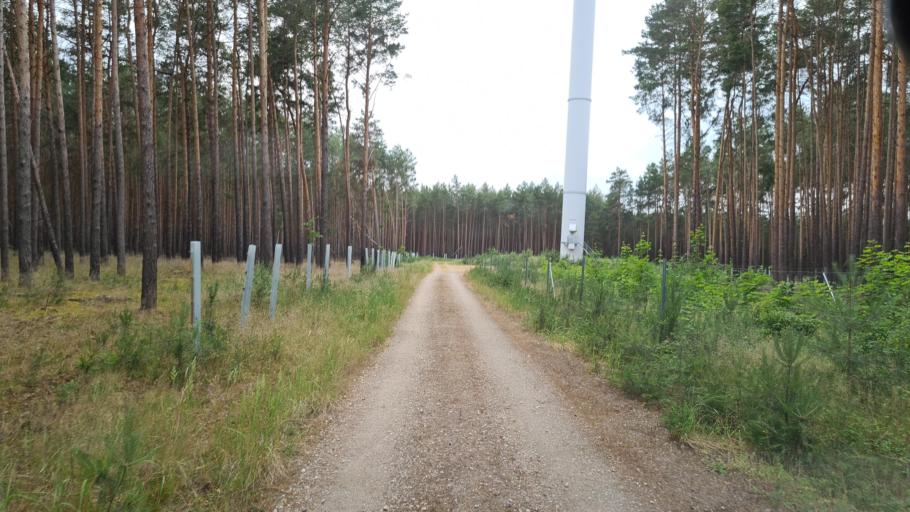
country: DE
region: Brandenburg
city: Schilda
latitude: 51.6506
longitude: 13.3639
